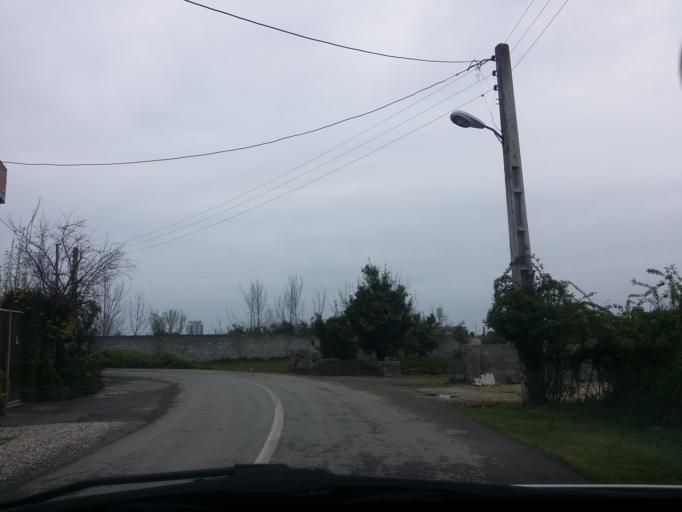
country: IR
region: Mazandaran
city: Chalus
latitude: 36.6759
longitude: 51.3792
